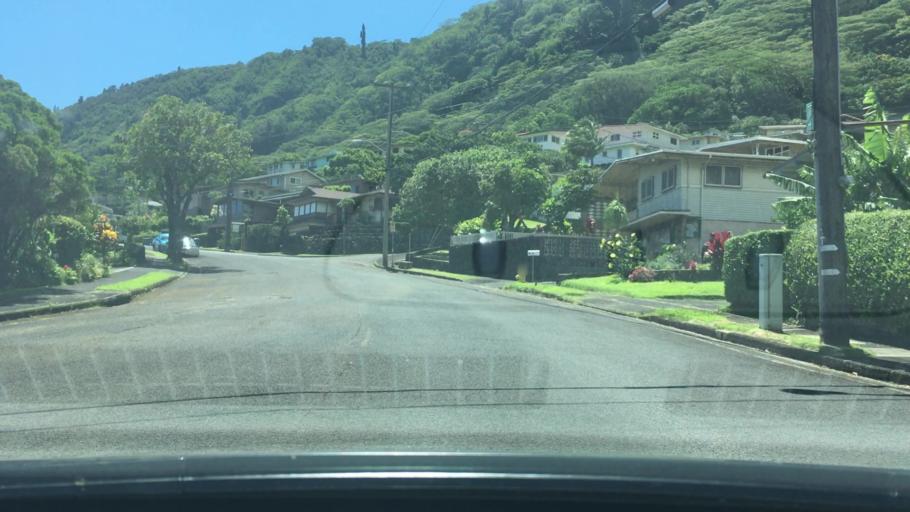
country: US
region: Hawaii
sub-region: Honolulu County
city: Honolulu
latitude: 21.3238
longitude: -157.8043
